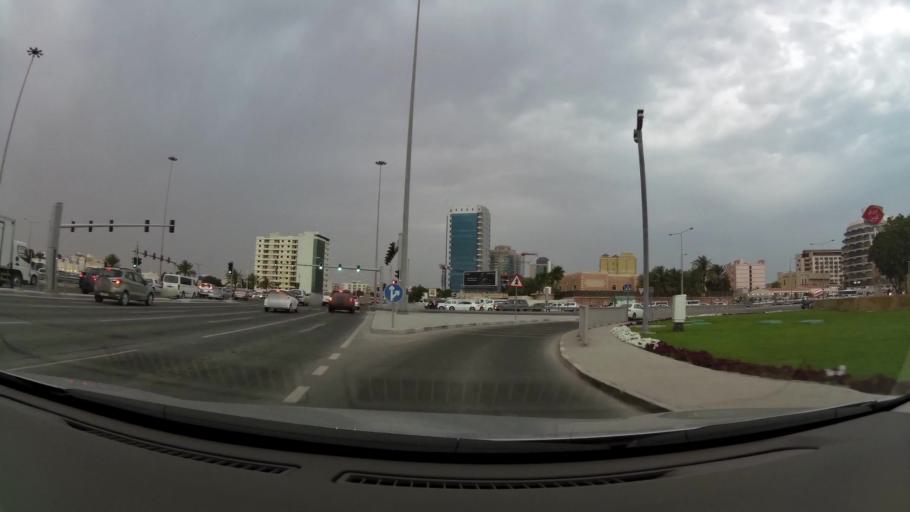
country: QA
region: Baladiyat ad Dawhah
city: Doha
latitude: 25.2722
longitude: 51.5114
